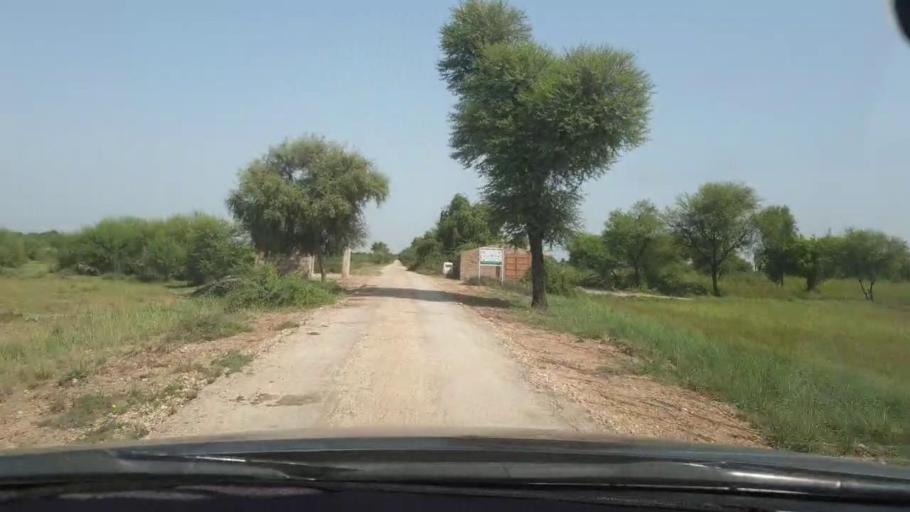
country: PK
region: Sindh
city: Naukot
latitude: 24.8132
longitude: 69.2555
